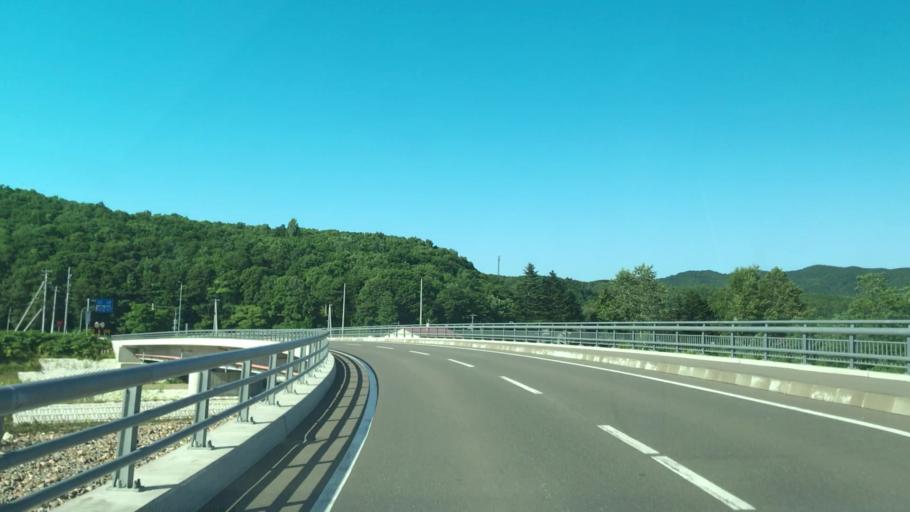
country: JP
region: Hokkaido
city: Yoichi
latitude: 43.0494
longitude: 140.8243
